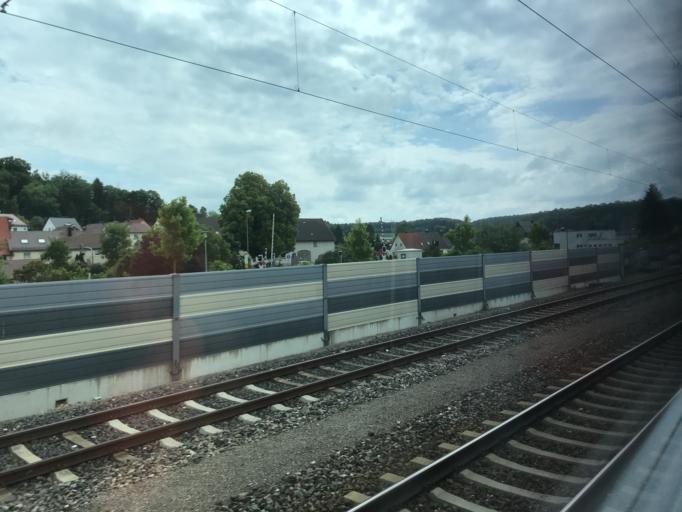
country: DE
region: Baden-Wuerttemberg
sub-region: Tuebingen Region
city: Amstetten
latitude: 48.5770
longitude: 9.8737
